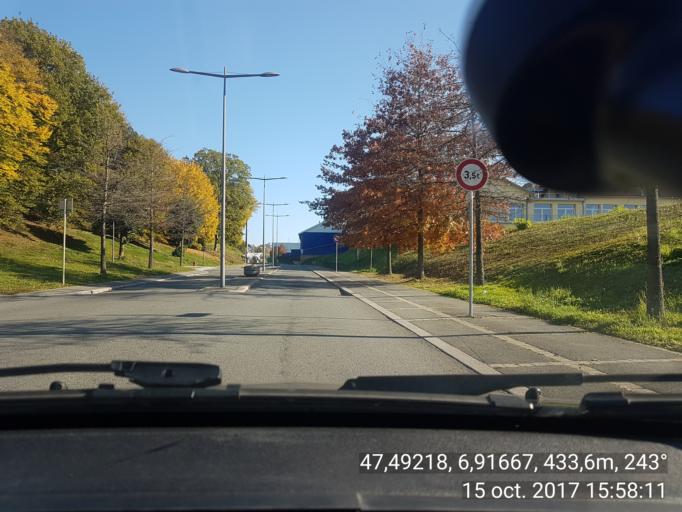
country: FR
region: Franche-Comte
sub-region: Territoire de Belfort
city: Beaucourt
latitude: 47.4922
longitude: 6.9165
